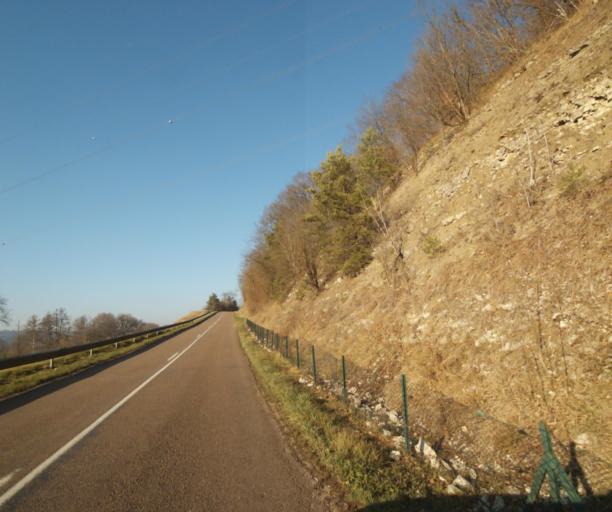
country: FR
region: Champagne-Ardenne
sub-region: Departement de la Haute-Marne
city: Chevillon
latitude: 48.5137
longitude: 5.1196
